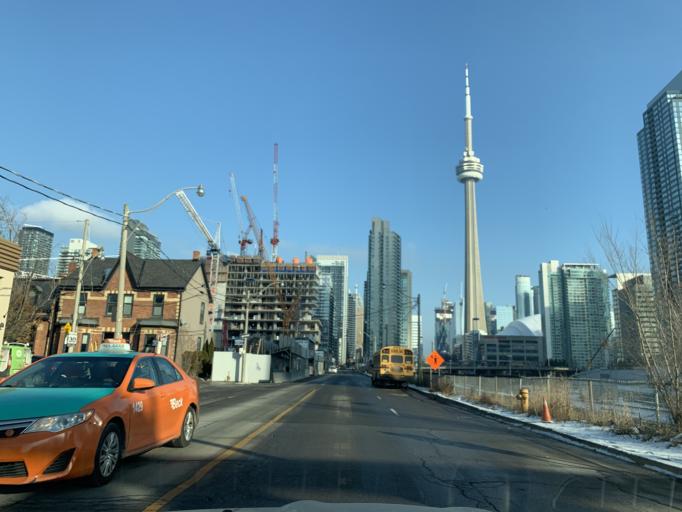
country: CA
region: Ontario
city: Toronto
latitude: 43.6416
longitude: -79.3979
